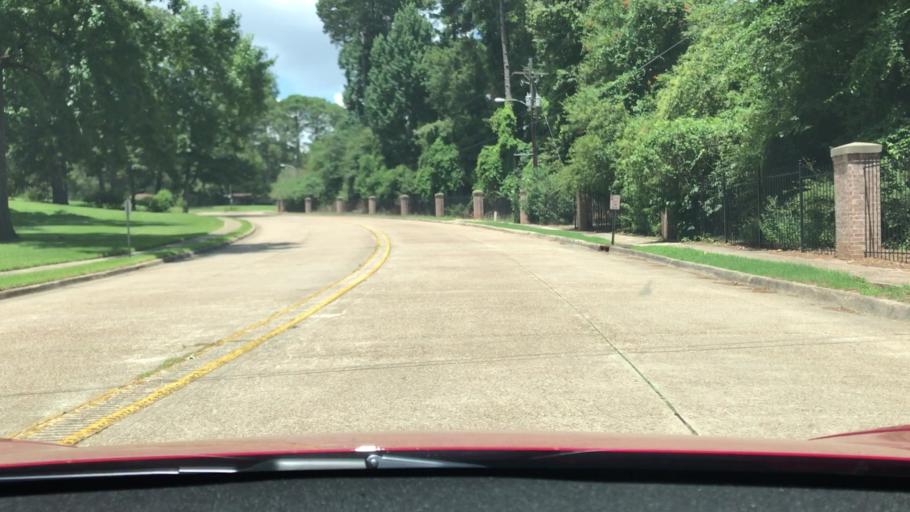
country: US
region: Louisiana
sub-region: Bossier Parish
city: Bossier City
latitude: 32.4354
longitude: -93.7307
